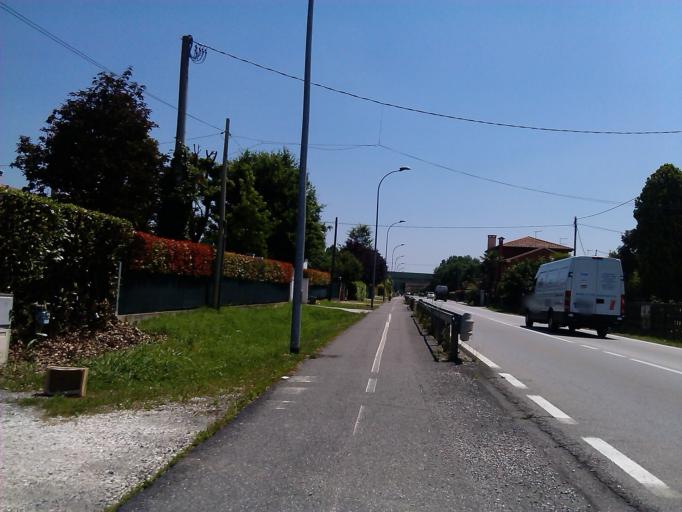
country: IT
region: Veneto
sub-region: Provincia di Padova
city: Camposampiero
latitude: 45.5605
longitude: 11.9476
